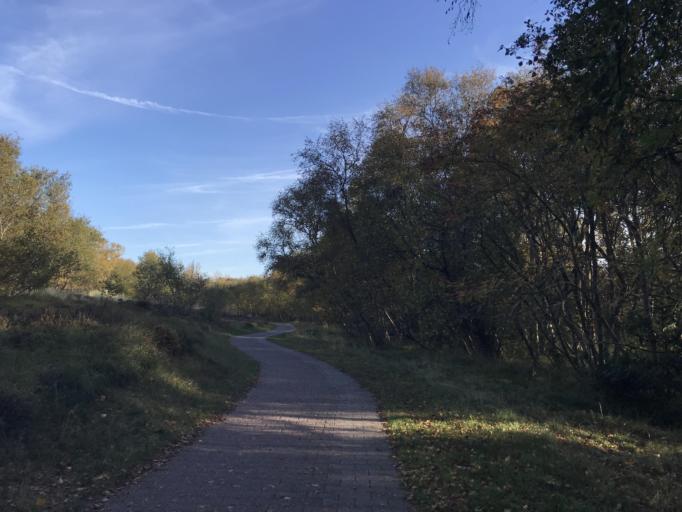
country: DE
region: Lower Saxony
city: Borkum
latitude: 53.5762
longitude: 6.6972
